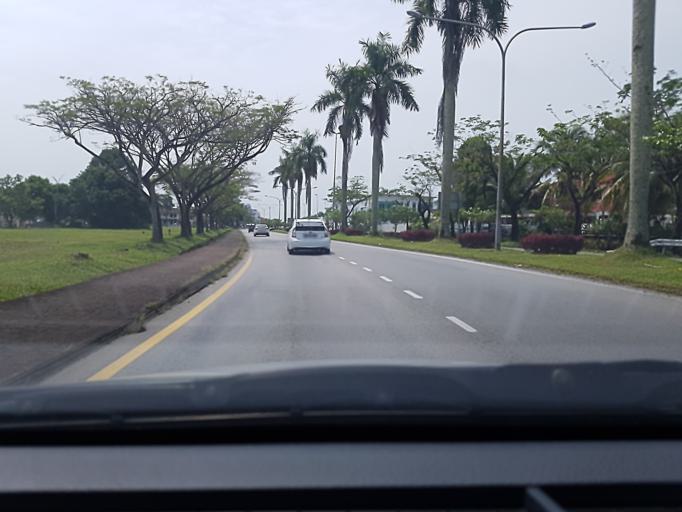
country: MY
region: Sarawak
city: Kuching
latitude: 1.5049
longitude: 110.3563
